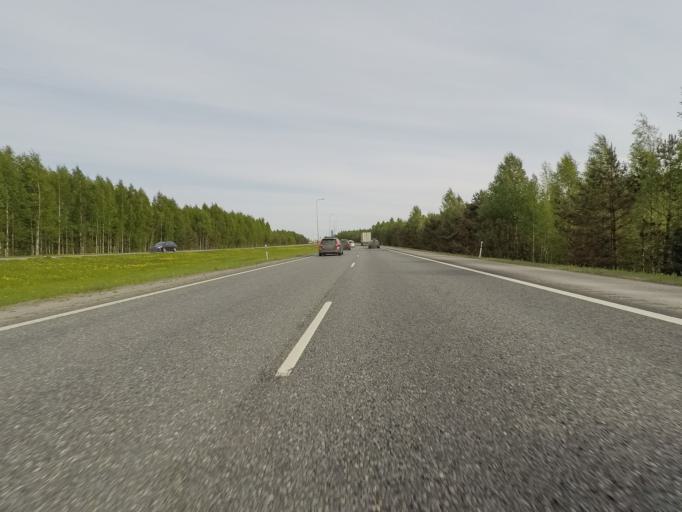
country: FI
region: Haeme
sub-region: Haemeenlinna
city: Janakkala
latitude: 60.8615
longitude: 24.5859
